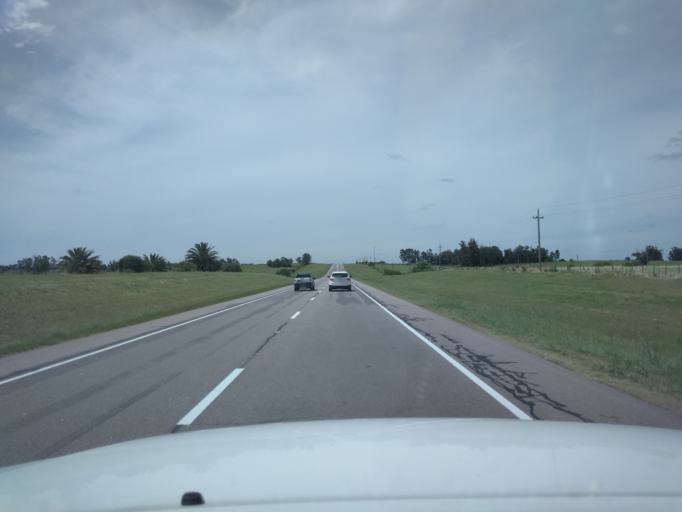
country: UY
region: Florida
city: Florida
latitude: -34.2191
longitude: -56.2084
